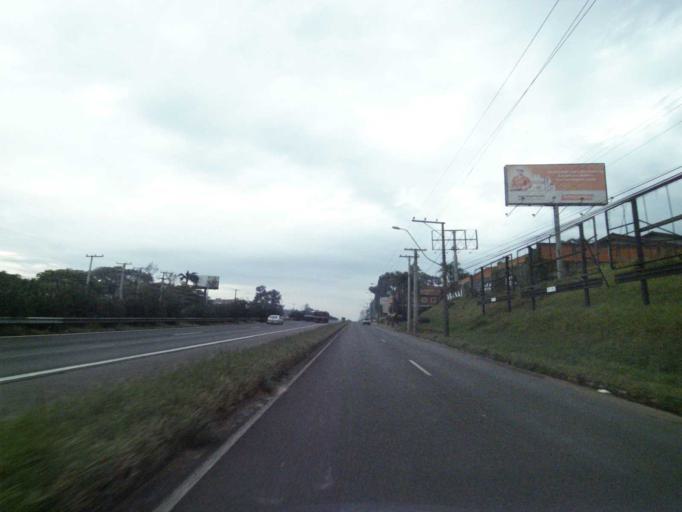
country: BR
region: Rio Grande do Sul
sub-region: Sao Leopoldo
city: Sao Leopoldo
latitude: -29.7935
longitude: -51.1648
